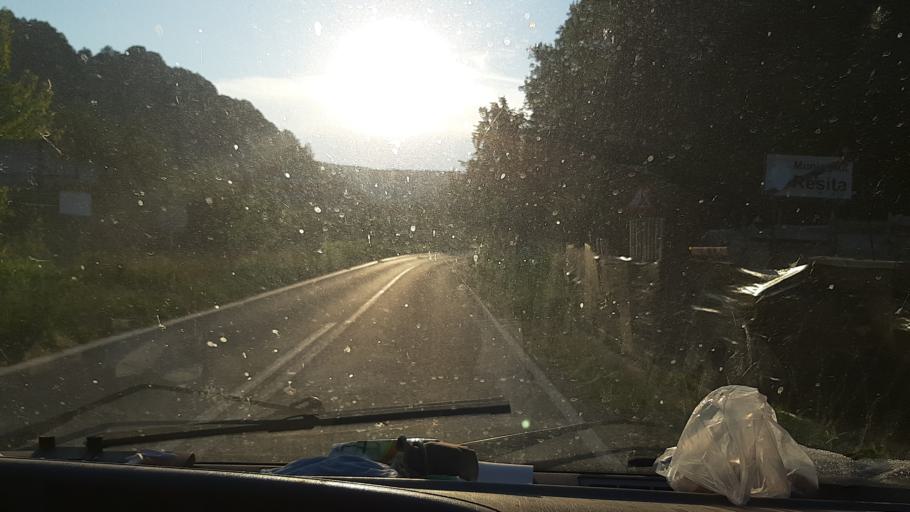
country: RO
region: Caras-Severin
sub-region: Municipiul Resita
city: Calnic
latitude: 45.3530
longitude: 21.8320
